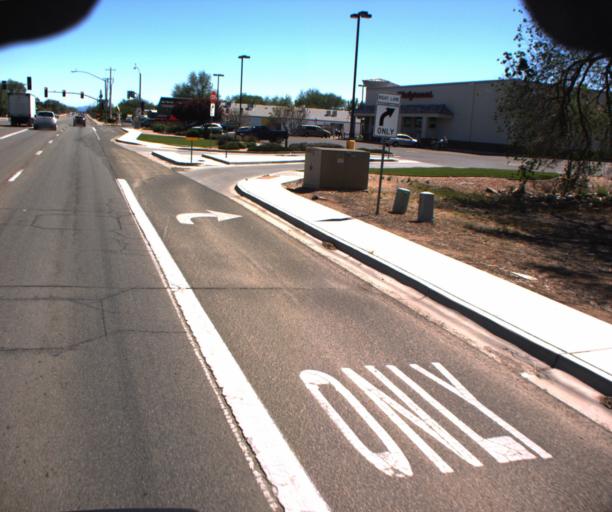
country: US
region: Arizona
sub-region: Yavapai County
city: Chino Valley
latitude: 34.7612
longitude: -112.4537
